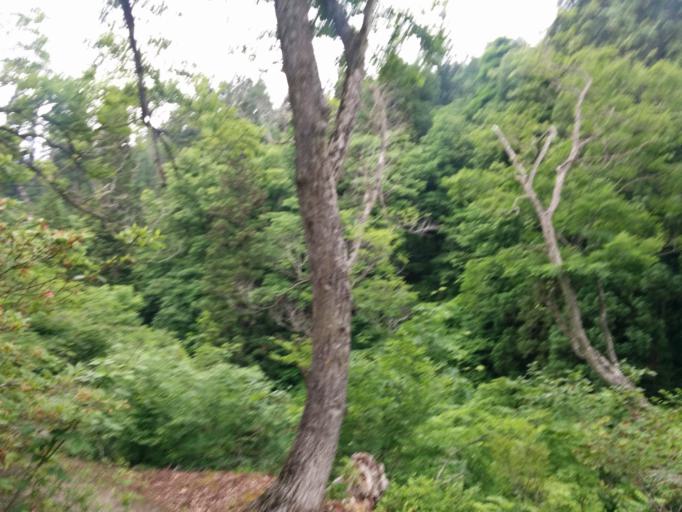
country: JP
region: Yamagata
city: Obanazawa
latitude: 38.5668
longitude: 140.5321
